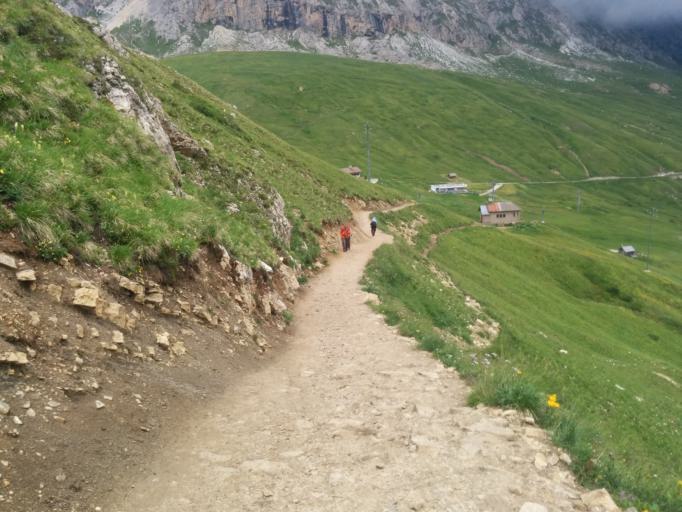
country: IT
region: Trentino-Alto Adige
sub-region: Provincia di Trento
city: Canazei
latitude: 46.4846
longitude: 11.8136
